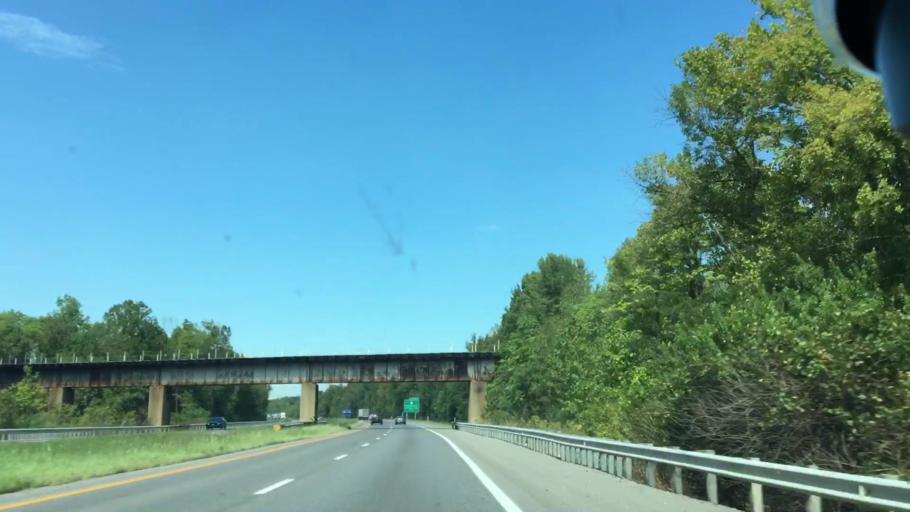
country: US
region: Kentucky
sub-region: Hopkins County
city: Madisonville
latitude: 37.3080
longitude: -87.4671
